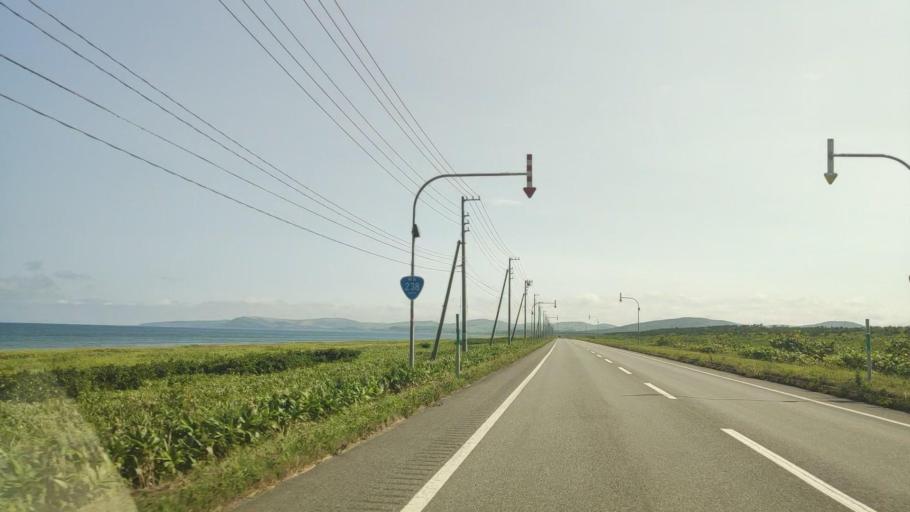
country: JP
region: Hokkaido
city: Makubetsu
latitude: 45.4104
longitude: 141.8136
